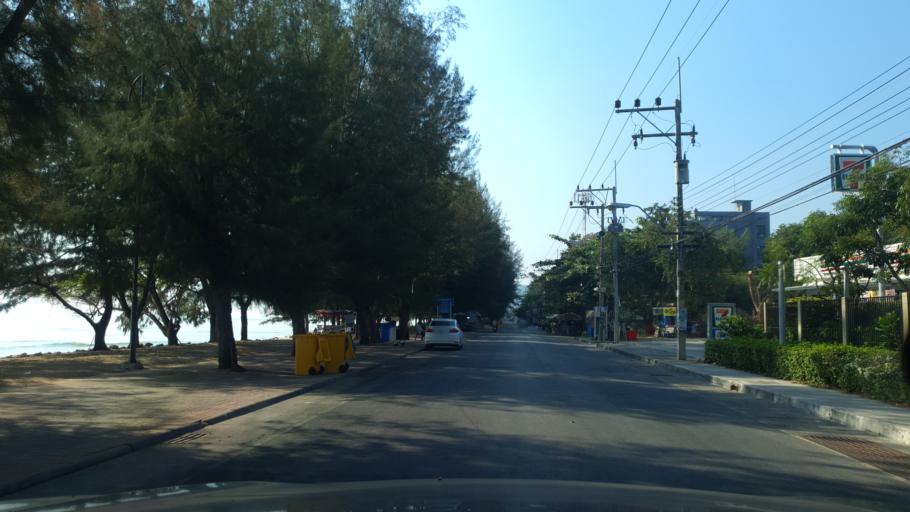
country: TH
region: Phetchaburi
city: Cha-am
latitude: 12.7787
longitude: 99.9779
